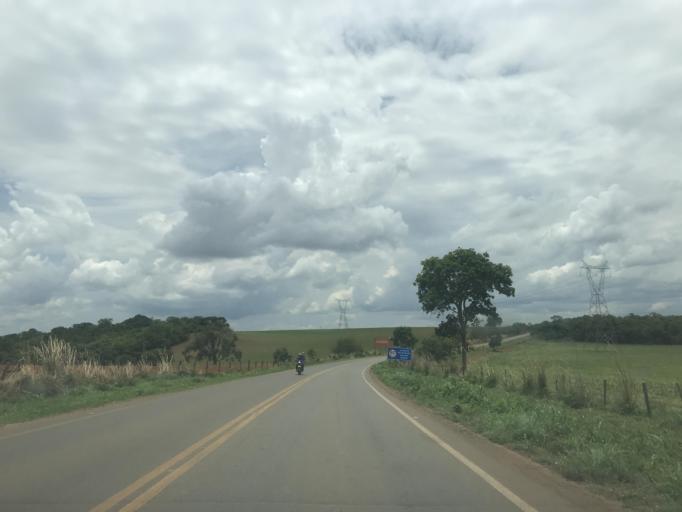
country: BR
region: Goias
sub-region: Vianopolis
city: Vianopolis
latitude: -16.7419
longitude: -48.4491
